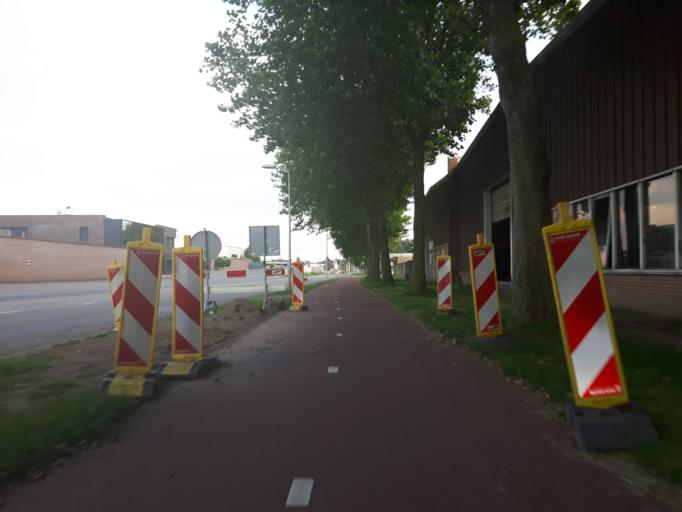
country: NL
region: Overijssel
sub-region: Gemeente Enschede
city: Enschede
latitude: 52.2232
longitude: 6.8456
